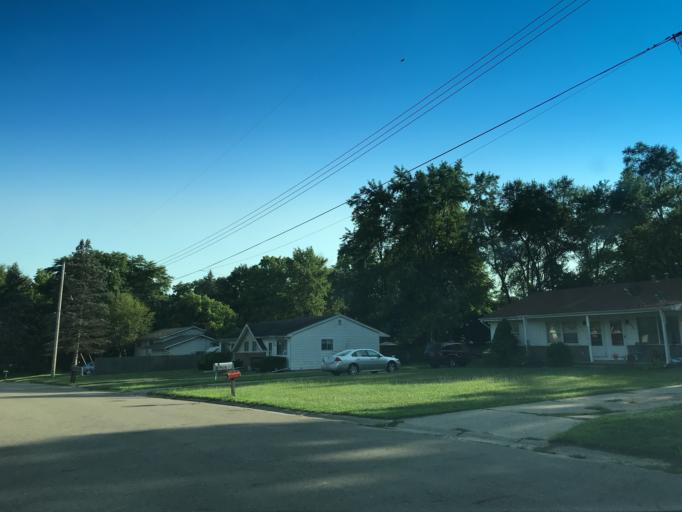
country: US
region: Michigan
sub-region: Eaton County
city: Waverly
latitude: 42.7043
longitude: -84.6181
